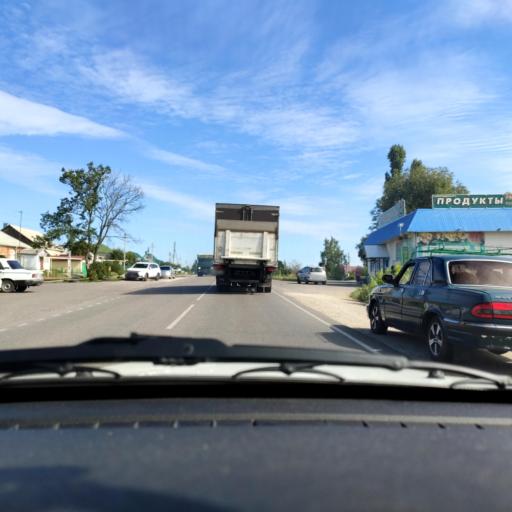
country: RU
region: Voronezj
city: Orlovo
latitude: 51.7536
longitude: 39.5880
